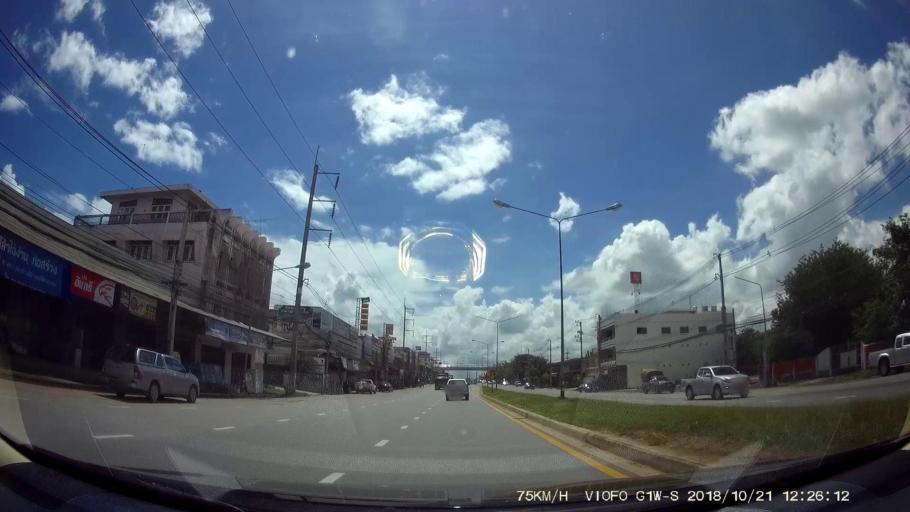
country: TH
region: Nakhon Ratchasima
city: Dan Khun Thot
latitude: 15.2121
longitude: 101.7684
